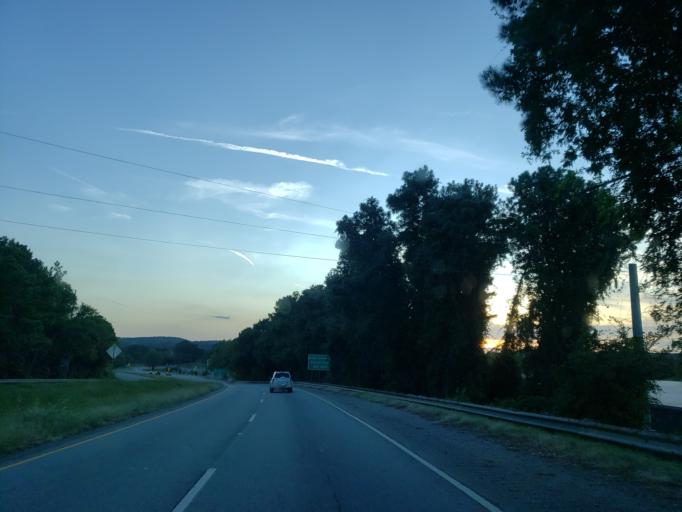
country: US
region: Georgia
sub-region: Floyd County
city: Rome
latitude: 34.2232
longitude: -85.1693
